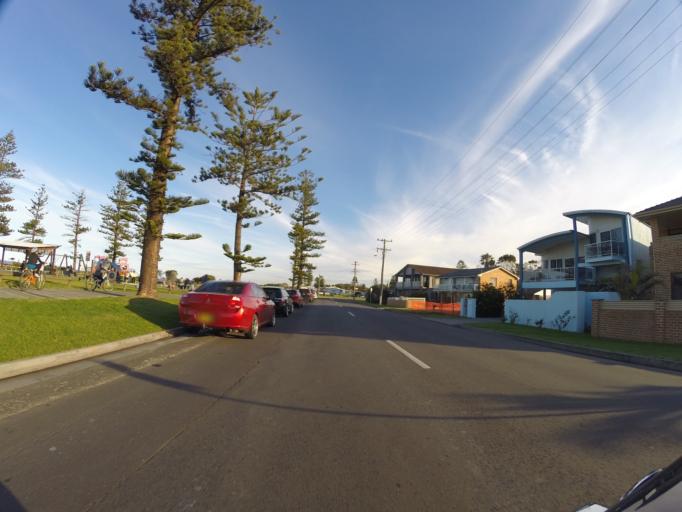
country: AU
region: New South Wales
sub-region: Wollongong
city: Bulli
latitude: -34.3392
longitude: 150.9246
